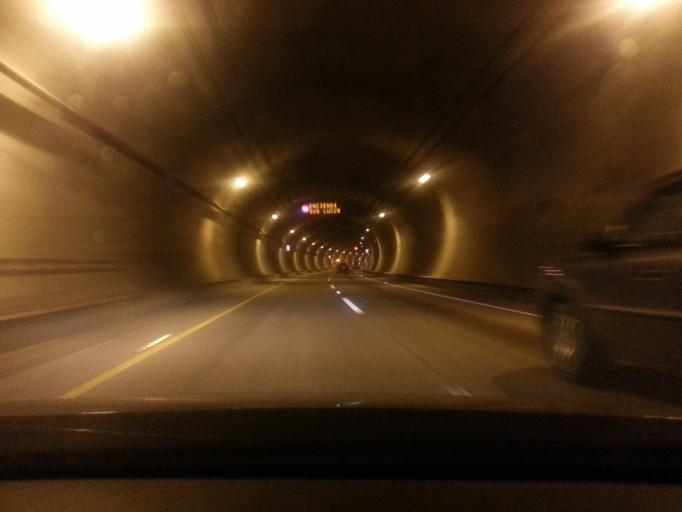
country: MX
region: Puebla
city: Xicotepec de Juarez
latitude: 20.3148
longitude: -97.9647
